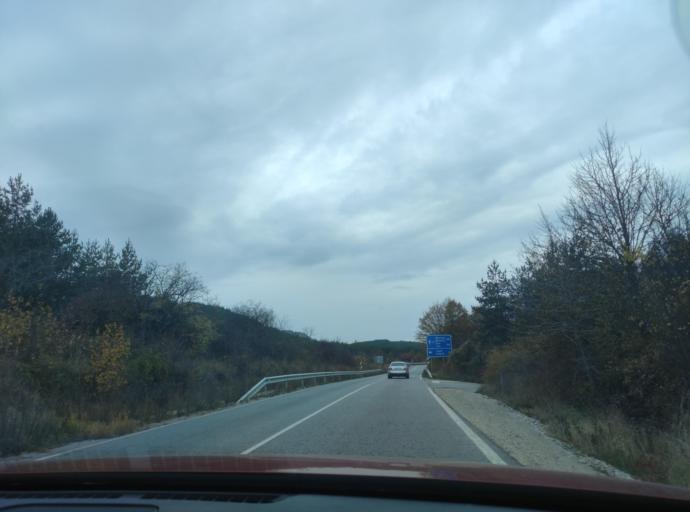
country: BG
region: Sofiya
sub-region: Obshtina Godech
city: Godech
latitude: 42.9807
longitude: 23.1317
